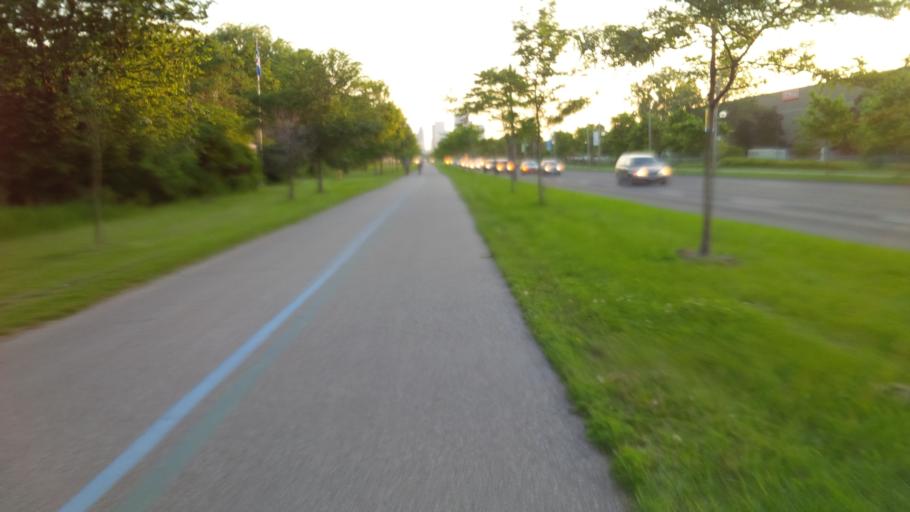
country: CA
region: Ontario
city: Toronto
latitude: 43.6613
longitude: -79.3187
